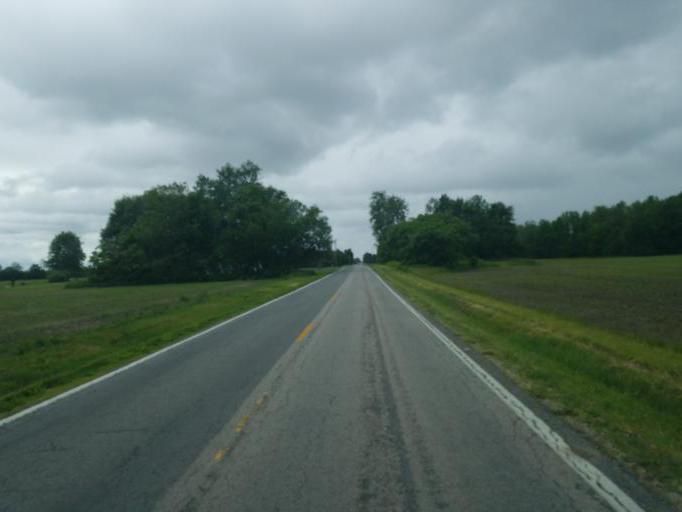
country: US
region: Ohio
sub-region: Morrow County
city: Cardington
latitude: 40.5318
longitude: -82.9827
